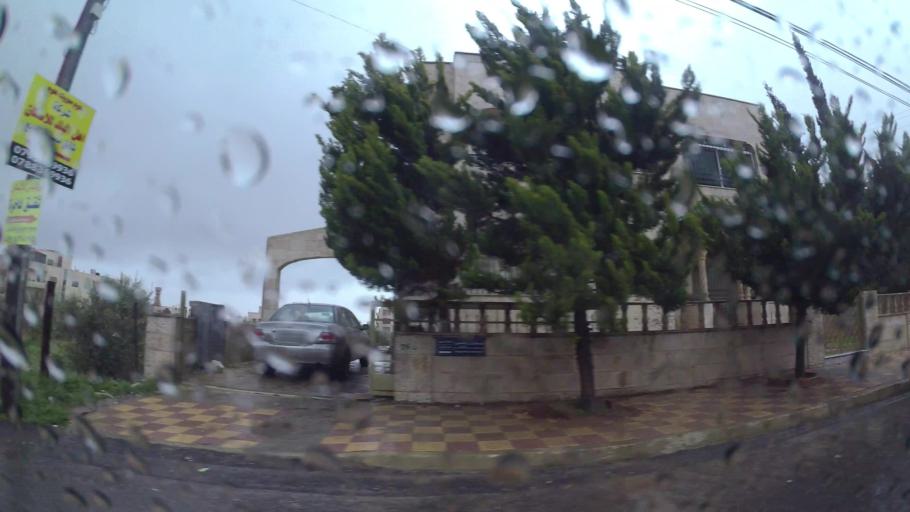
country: JO
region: Amman
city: Al Jubayhah
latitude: 32.0353
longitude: 35.8823
